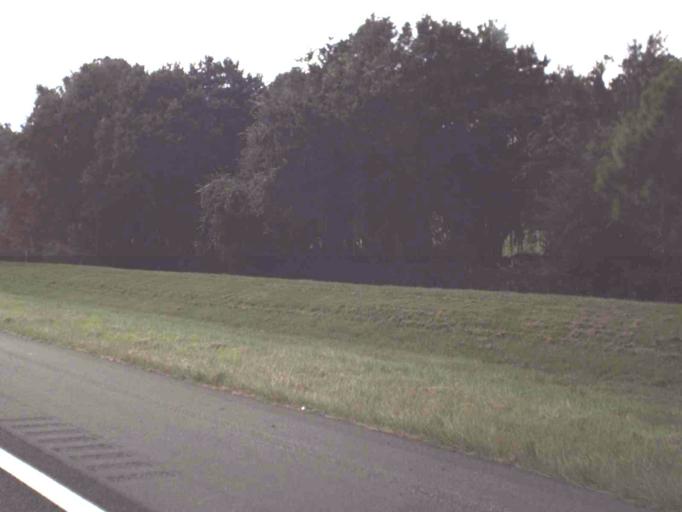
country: US
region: Florida
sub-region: Polk County
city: Fussels Corner
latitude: 28.0246
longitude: -81.8316
